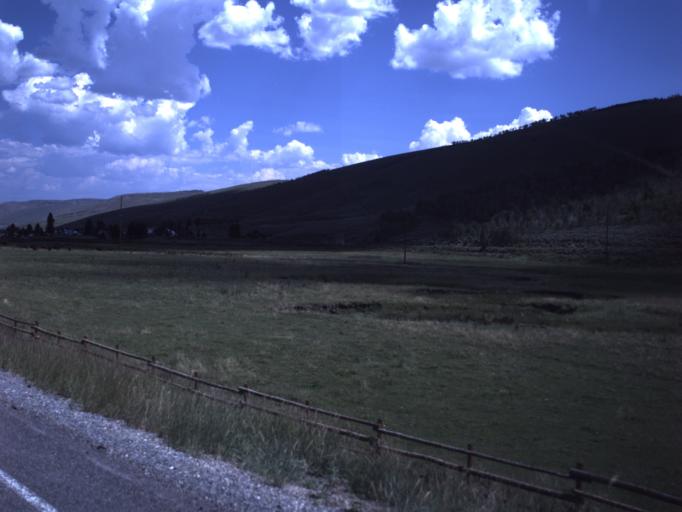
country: US
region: Utah
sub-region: Sanpete County
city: Fairview
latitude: 39.7172
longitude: -111.1632
